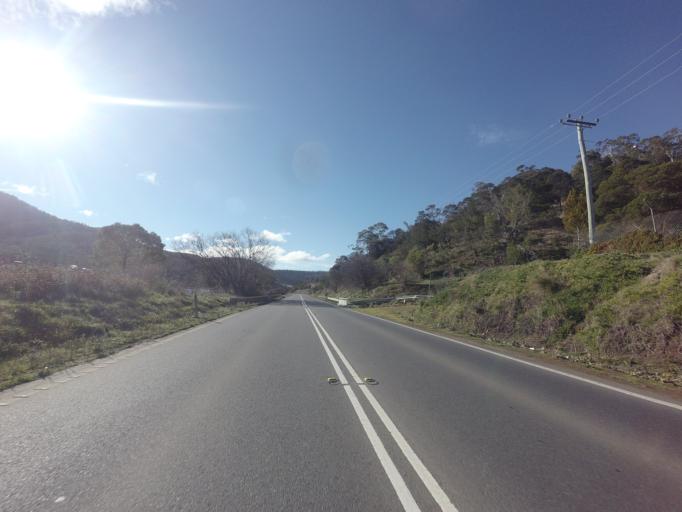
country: AU
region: Tasmania
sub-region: Glenorchy
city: Granton
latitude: -42.7671
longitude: 147.1435
